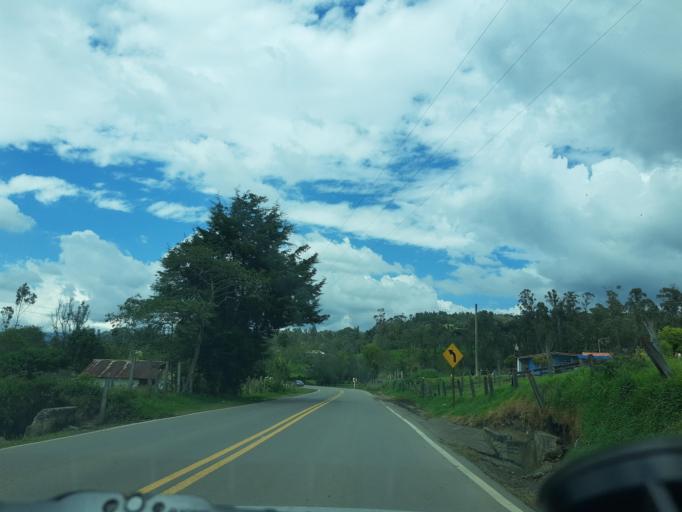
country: CO
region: Boyaca
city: Chiquinquira
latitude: 5.6178
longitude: -73.7470
